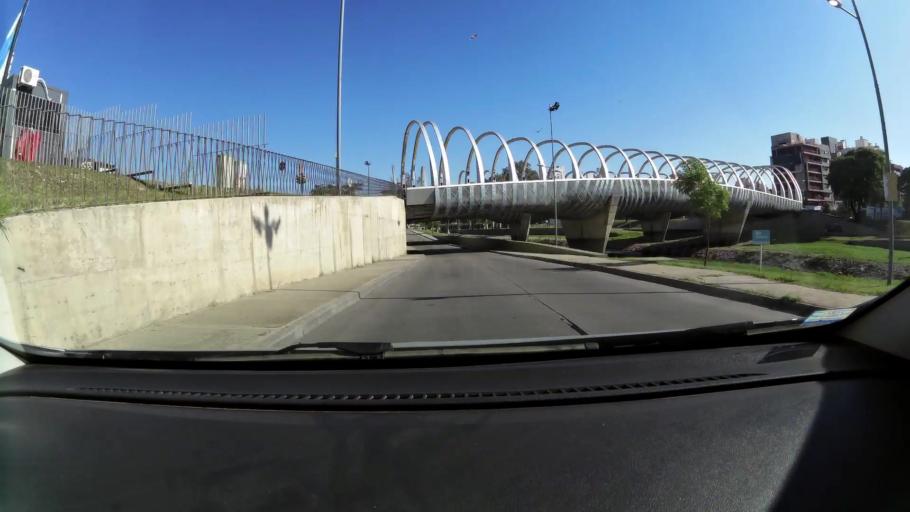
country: AR
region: Cordoba
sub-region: Departamento de Capital
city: Cordoba
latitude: -31.4185
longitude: -64.1733
